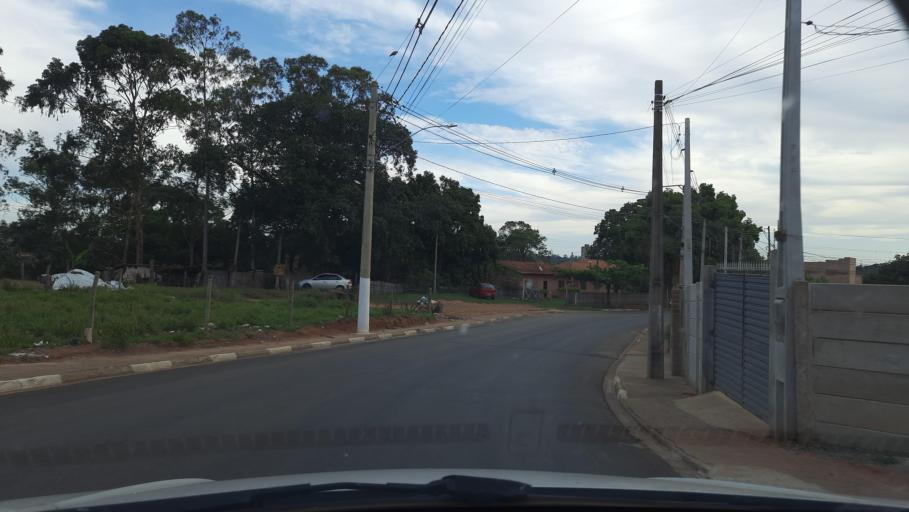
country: BR
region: Sao Paulo
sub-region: Casa Branca
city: Casa Branca
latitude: -21.7638
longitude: -47.0857
